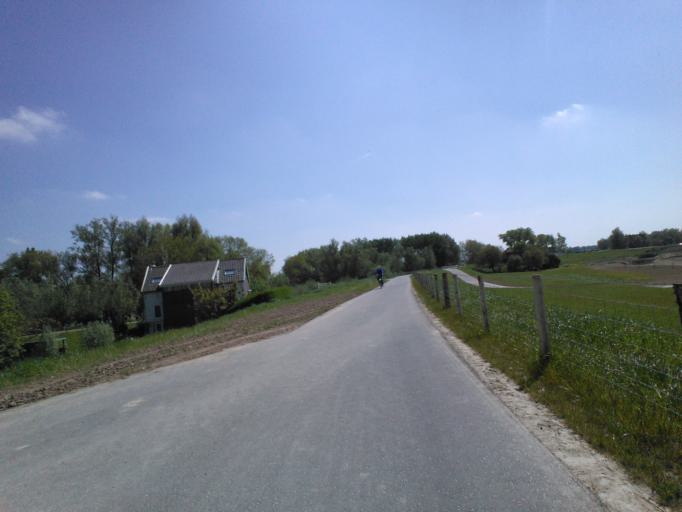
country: NL
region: South Holland
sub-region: Gemeente Sliedrecht
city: Sliedrecht
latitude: 51.7917
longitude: 4.7565
